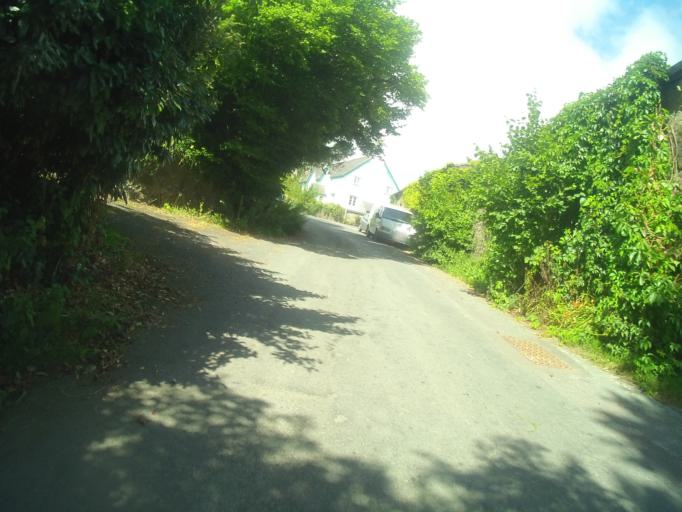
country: GB
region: England
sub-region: Devon
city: Buckfastleigh
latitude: 50.5110
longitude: -3.8251
